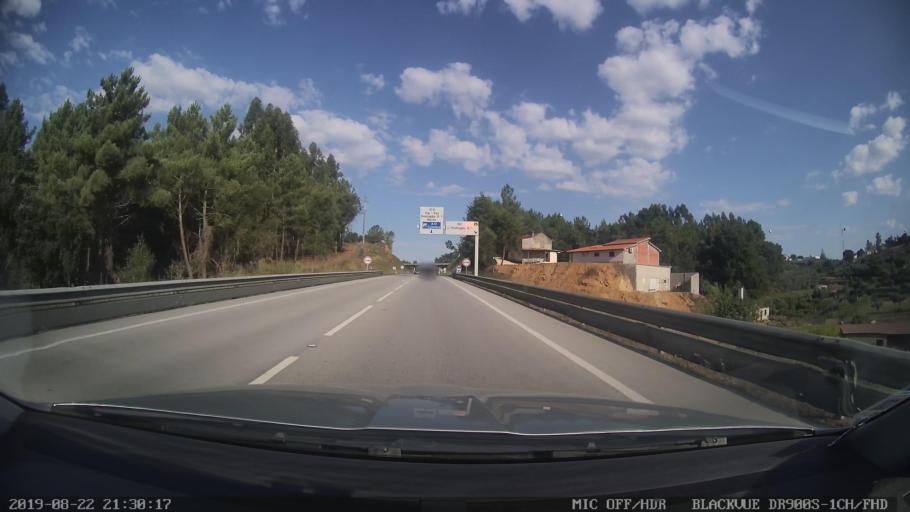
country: PT
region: Leiria
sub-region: Pedrogao Grande
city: Pedrogao Grande
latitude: 39.9087
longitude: -8.1487
